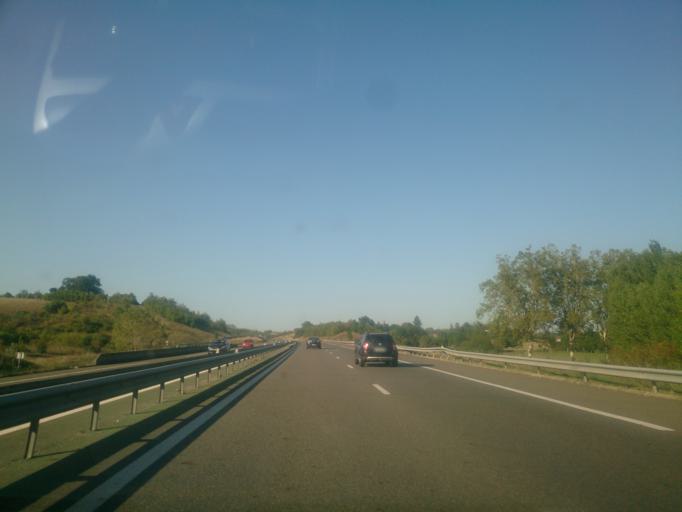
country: FR
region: Midi-Pyrenees
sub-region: Departement du Tarn-et-Garonne
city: Caussade
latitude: 44.1677
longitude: 1.5252
